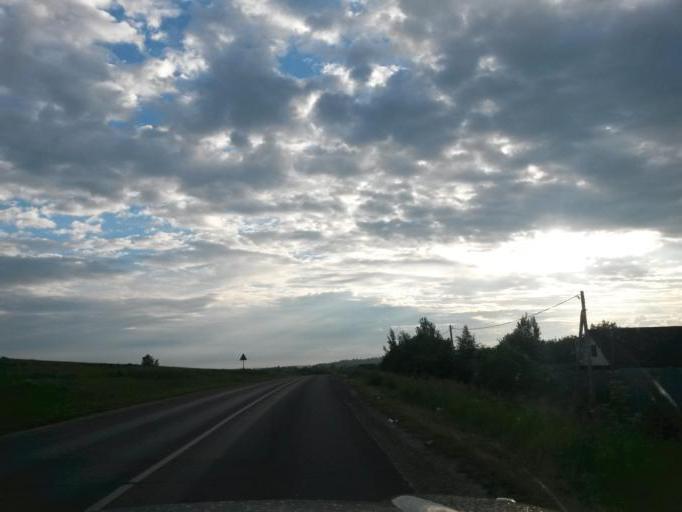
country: RU
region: Moskovskaya
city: Lyubuchany
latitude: 55.2941
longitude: 37.6304
